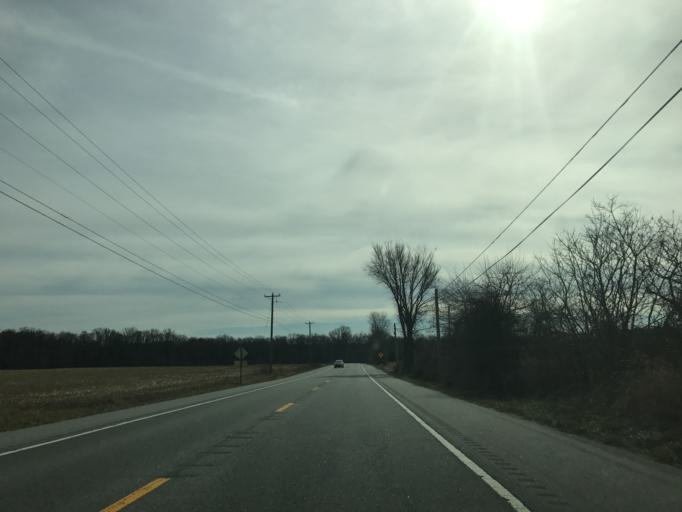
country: US
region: Maryland
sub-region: Queen Anne's County
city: Centreville
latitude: 39.0838
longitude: -76.0331
